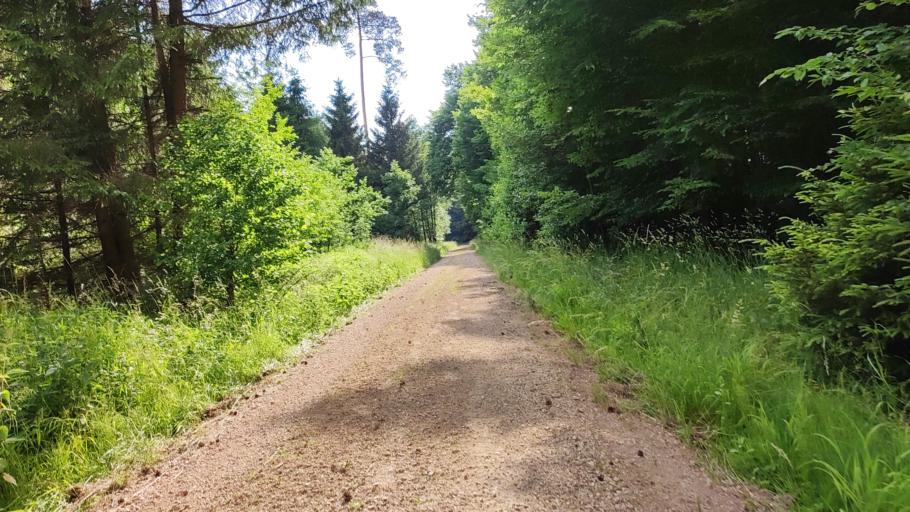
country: DE
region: Bavaria
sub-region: Swabia
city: Landensberg
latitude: 48.4252
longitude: 10.5528
